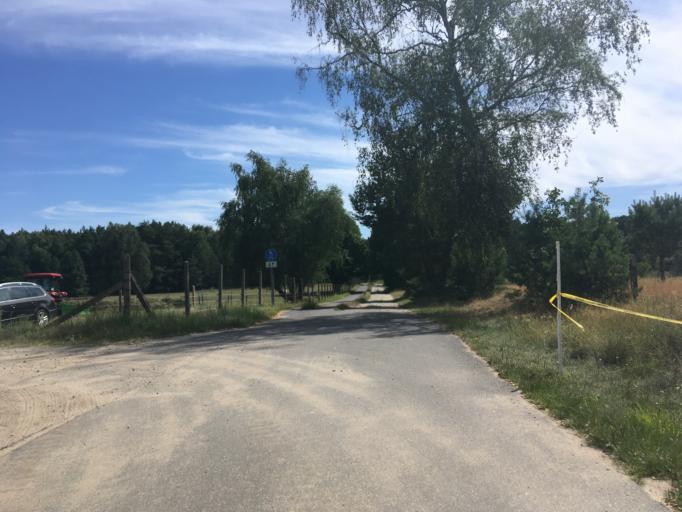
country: DE
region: Brandenburg
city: Rheinsberg
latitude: 53.0814
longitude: 12.9029
